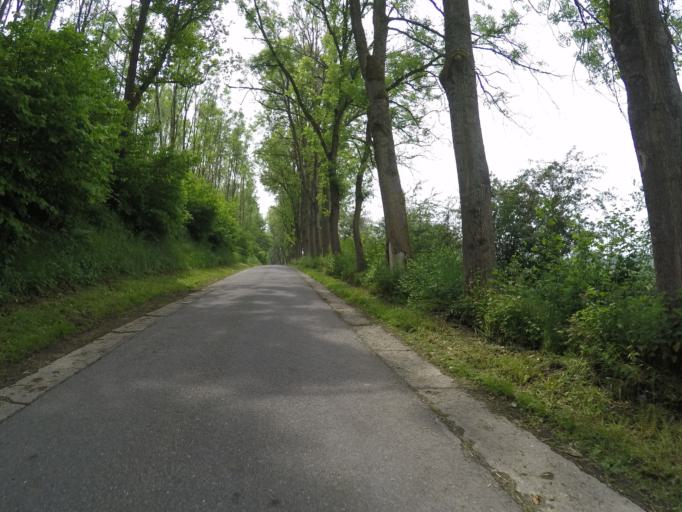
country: BE
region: Wallonia
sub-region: Province de Namur
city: Ciney
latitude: 50.3207
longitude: 5.0733
